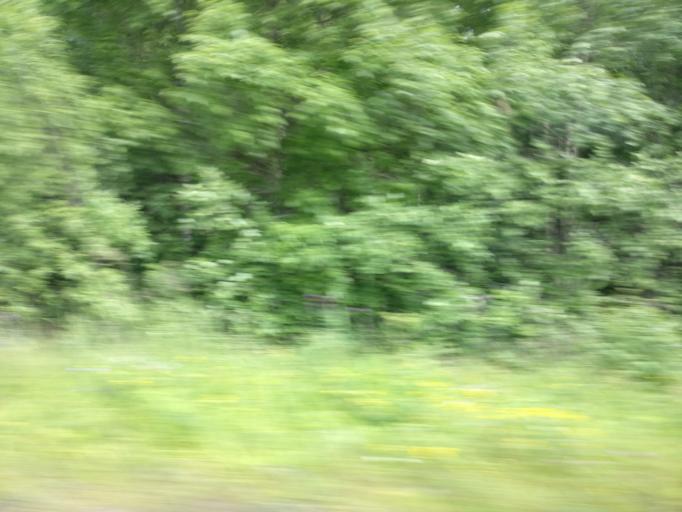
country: FI
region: Northern Savo
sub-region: Koillis-Savo
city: Juankoski
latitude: 62.9269
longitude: 28.2130
